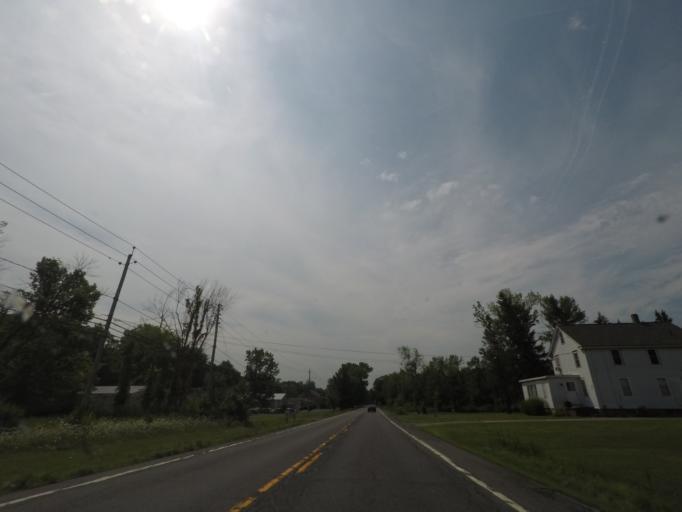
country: US
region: New York
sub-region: Saratoga County
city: Mechanicville
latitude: 42.8745
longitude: -73.6791
